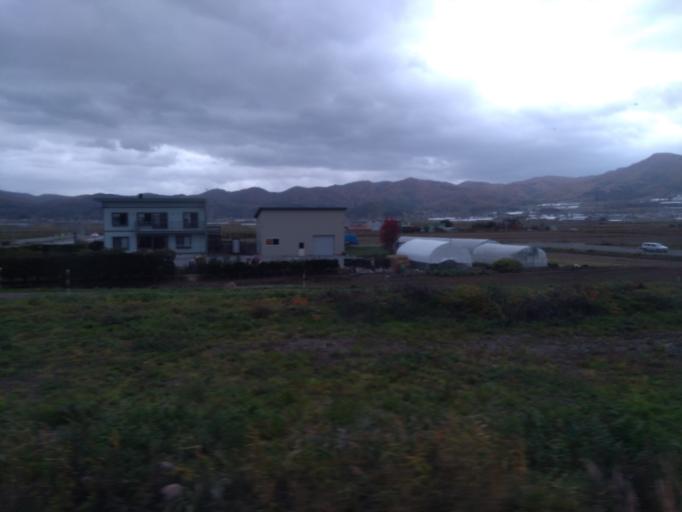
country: JP
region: Hokkaido
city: Nanae
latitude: 41.9032
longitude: 140.6554
